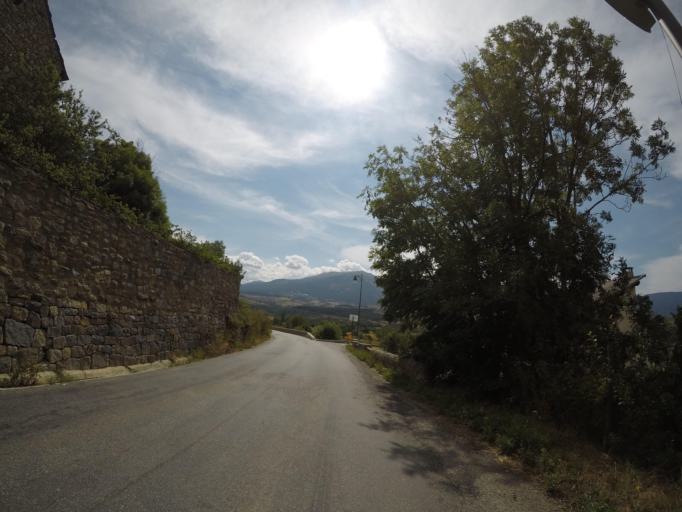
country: ES
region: Catalonia
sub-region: Provincia de Girona
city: Llivia
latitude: 42.4884
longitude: 2.0413
